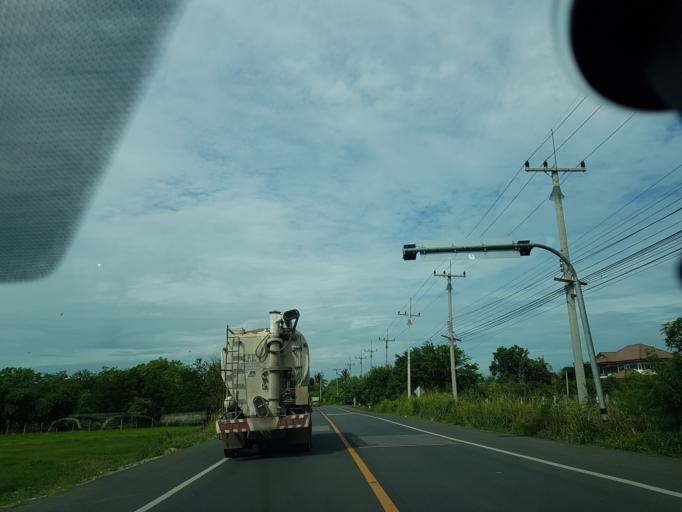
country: TH
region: Lop Buri
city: Tha Wung
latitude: 14.7694
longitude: 100.5667
